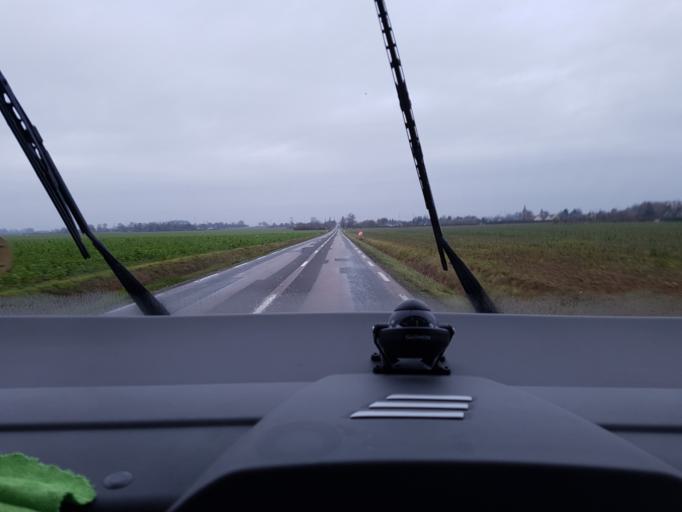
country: FR
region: Haute-Normandie
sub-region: Departement de l'Eure
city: Beaumont-le-Roger
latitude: 49.1062
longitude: 0.8317
